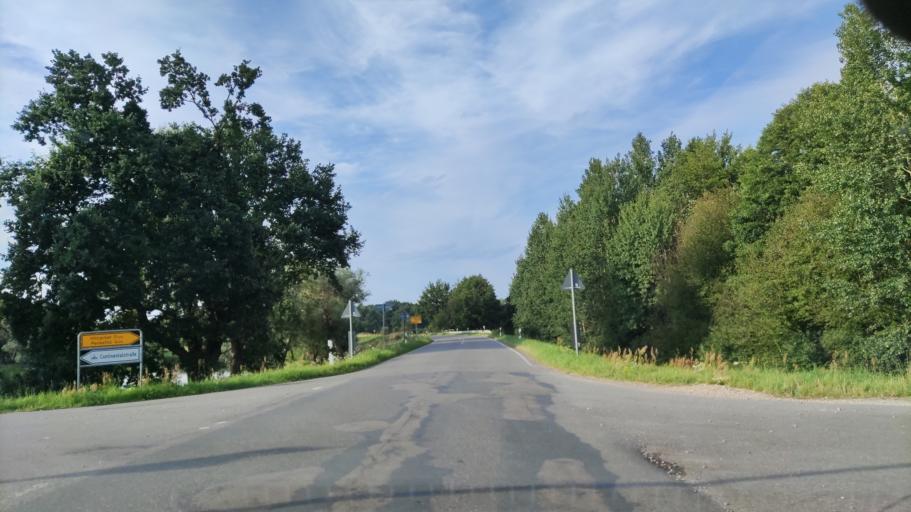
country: DE
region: Lower Saxony
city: Dannenberg
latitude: 53.1068
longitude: 11.1099
